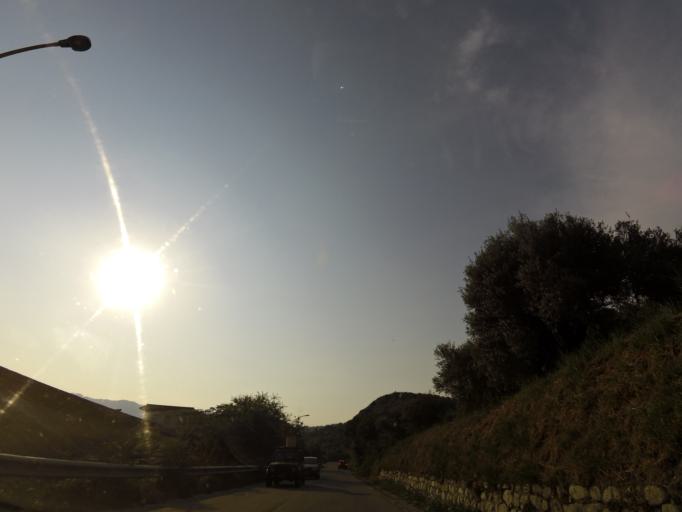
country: IT
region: Calabria
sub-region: Provincia di Catanzaro
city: Guardavalle
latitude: 38.4653
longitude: 16.5103
